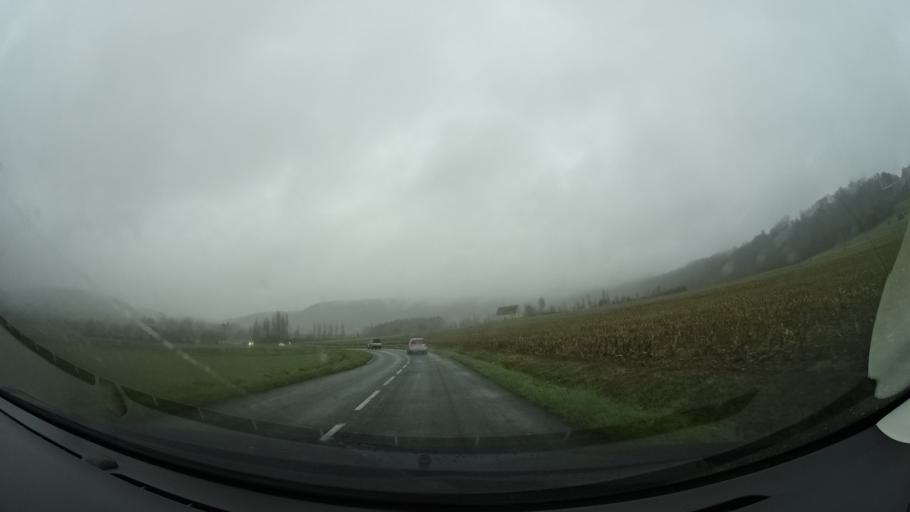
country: FR
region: Aquitaine
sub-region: Departement de la Dordogne
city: Cenac-et-Saint-Julien
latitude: 44.8267
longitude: 1.1587
